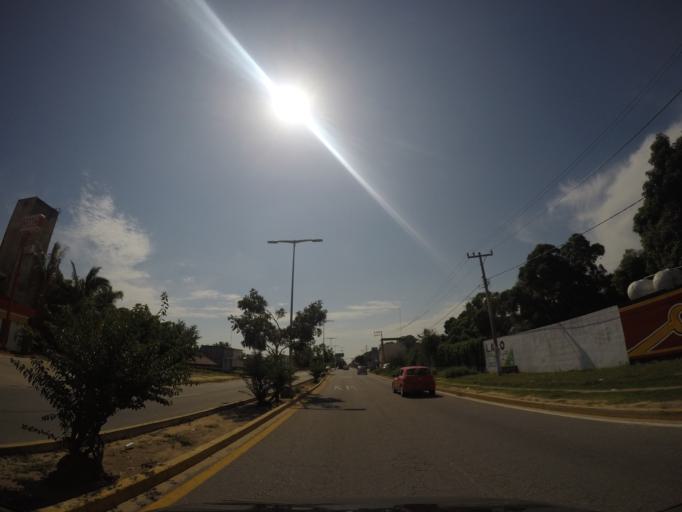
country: MX
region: Oaxaca
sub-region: San Pedro Mixtepec -Dto. 22 -
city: Puerto Escondido
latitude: 15.8671
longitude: -97.0786
